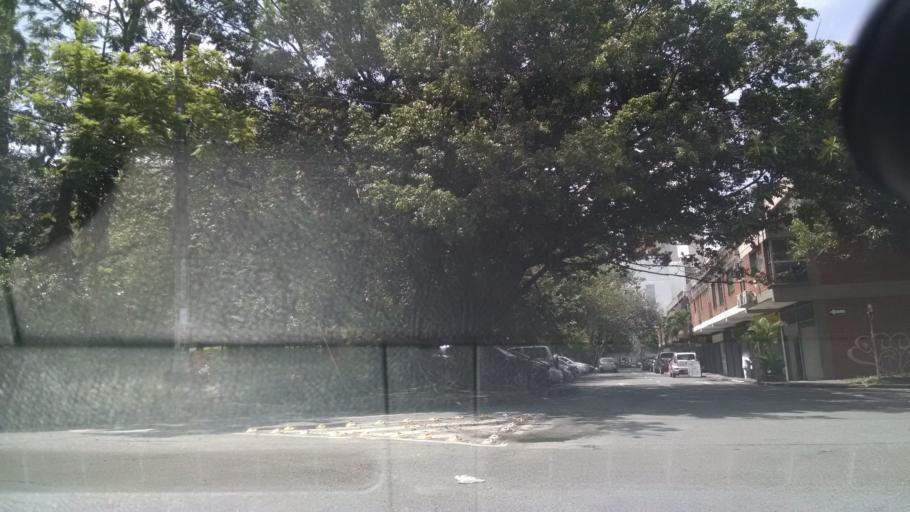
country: CO
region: Antioquia
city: Medellin
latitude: 6.2315
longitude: -75.5685
